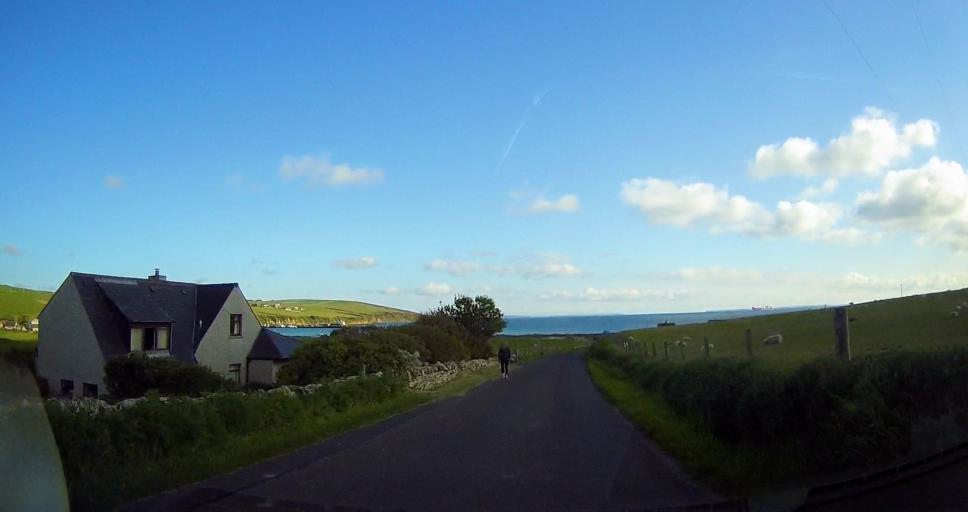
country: GB
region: Scotland
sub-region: Orkney Islands
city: Orkney
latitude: 58.9656
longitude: -2.9772
